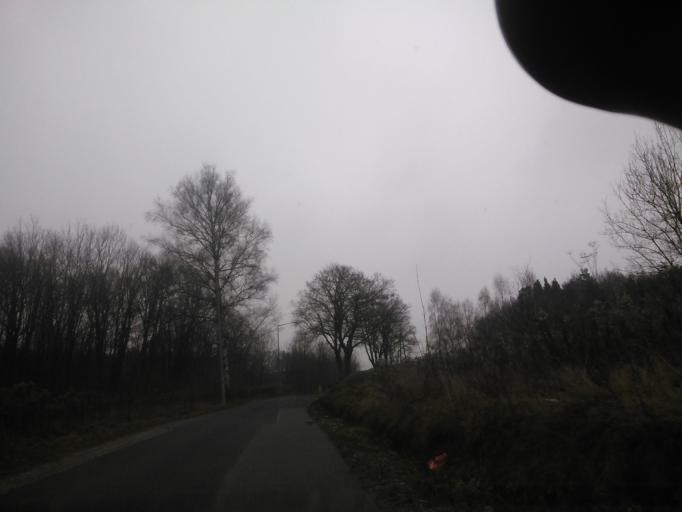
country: PL
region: Lower Silesian Voivodeship
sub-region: Jelenia Gora
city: Cieplice Slaskie Zdroj
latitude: 50.8597
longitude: 15.7005
